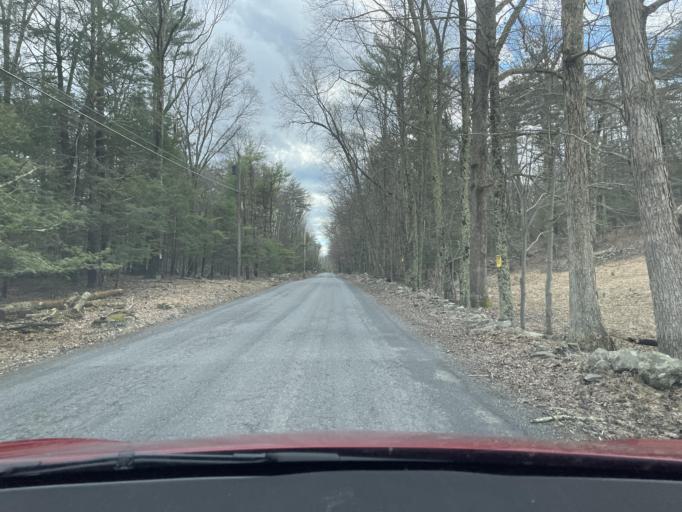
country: US
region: New York
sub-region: Ulster County
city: Zena
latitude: 42.0264
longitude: -74.0512
